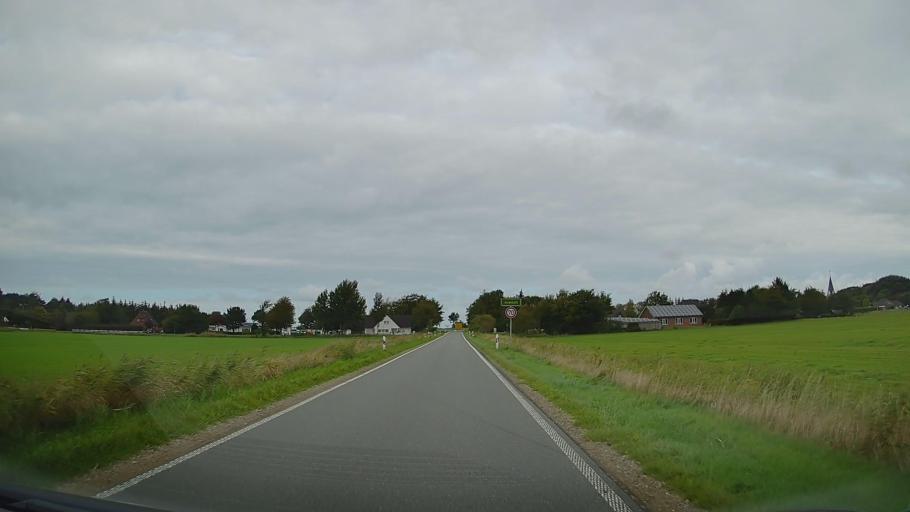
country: DE
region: Schleswig-Holstein
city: Aventoft
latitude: 54.8978
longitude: 8.8086
